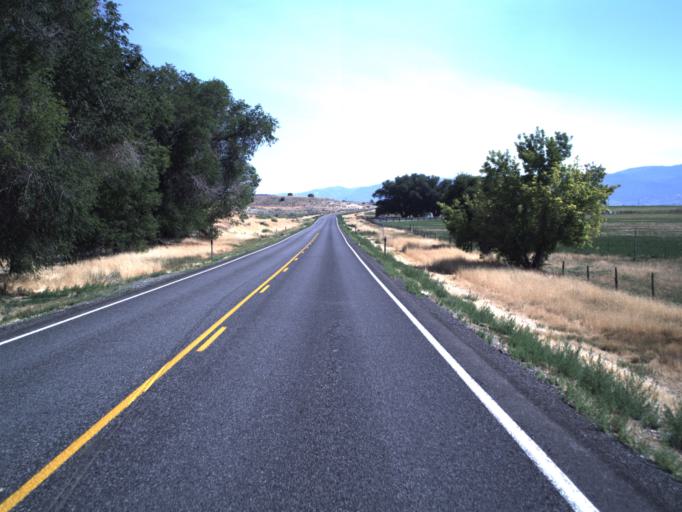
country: US
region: Utah
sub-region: Sanpete County
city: Moroni
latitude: 39.5309
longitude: -111.5444
